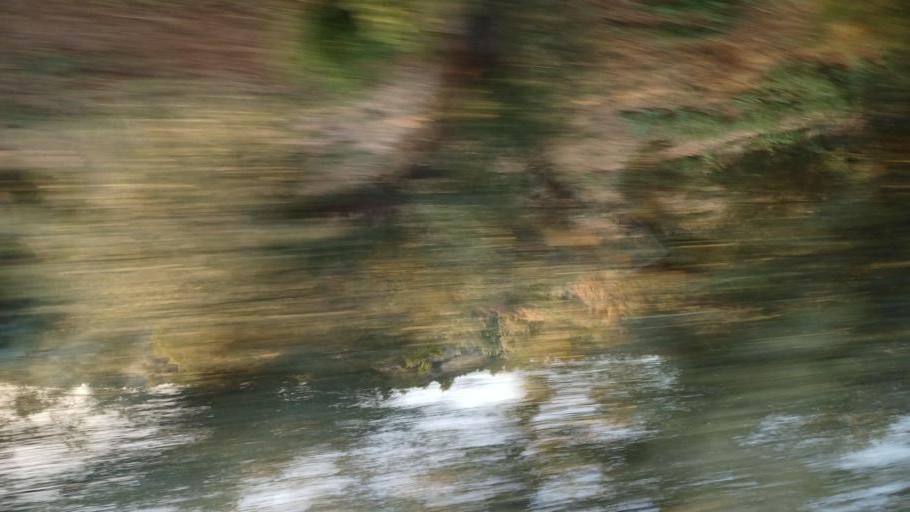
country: CY
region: Lefkosia
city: Lythrodontas
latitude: 34.9484
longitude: 33.2704
